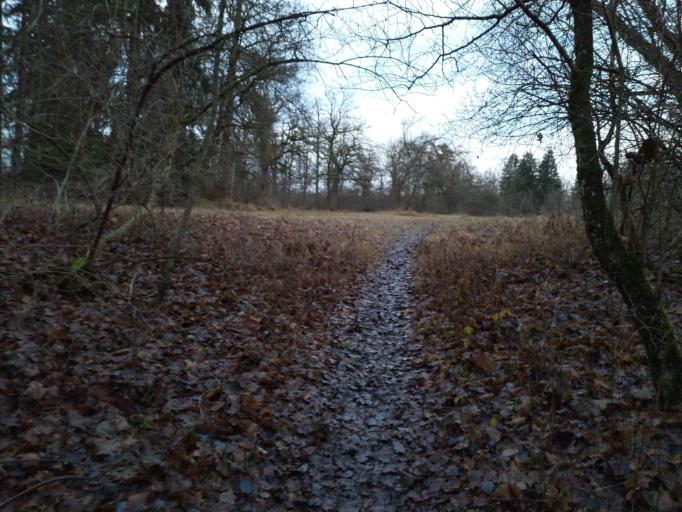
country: DE
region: Bavaria
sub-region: Swabia
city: Guenzburg
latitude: 48.4742
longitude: 10.3060
